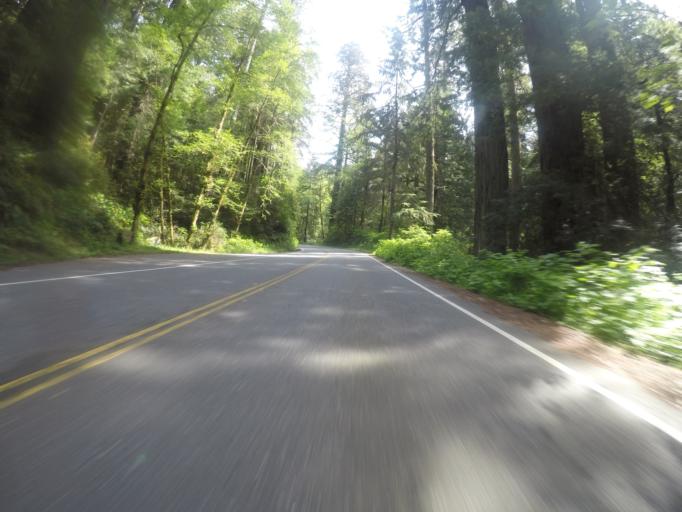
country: US
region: California
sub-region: Del Norte County
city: Bertsch-Oceanview
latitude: 41.4460
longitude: -124.0409
